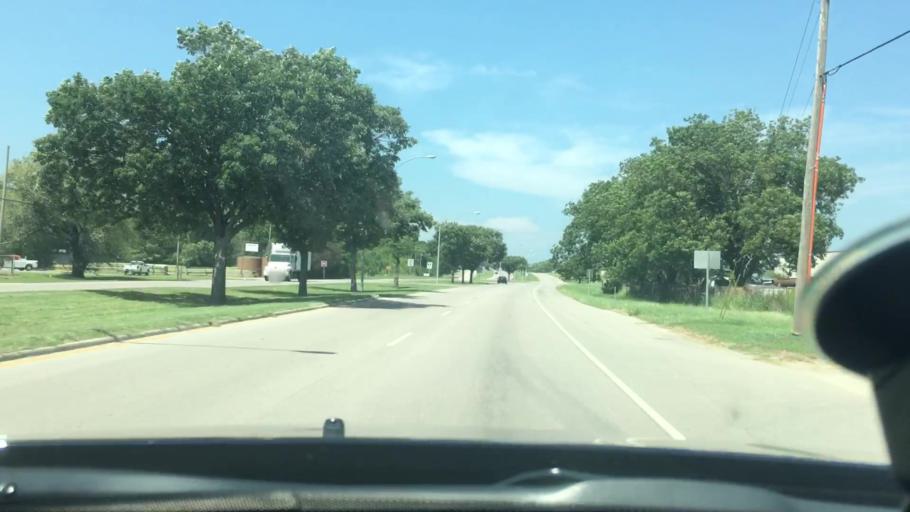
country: US
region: Oklahoma
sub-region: Pontotoc County
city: Ada
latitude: 34.7983
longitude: -96.6786
